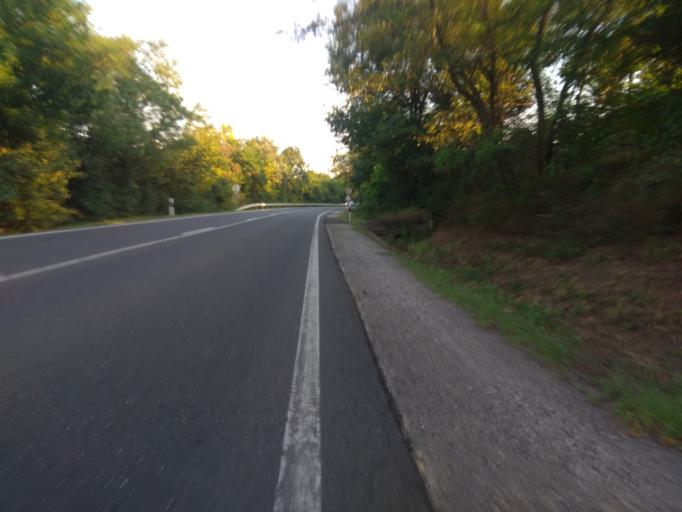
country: HU
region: Borsod-Abauj-Zemplen
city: Nyekladhaza
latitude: 47.9600
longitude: 20.8346
